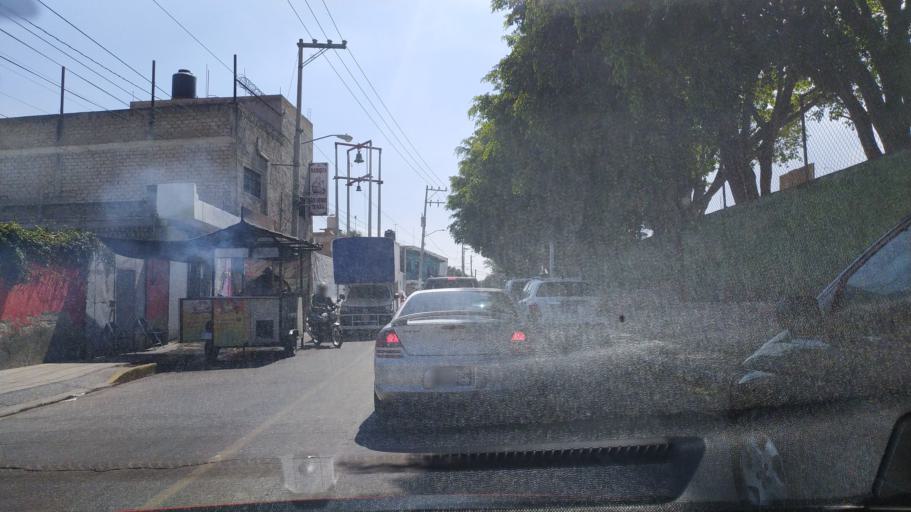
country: MX
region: Jalisco
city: Nuevo Mexico
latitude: 20.7688
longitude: -103.4392
